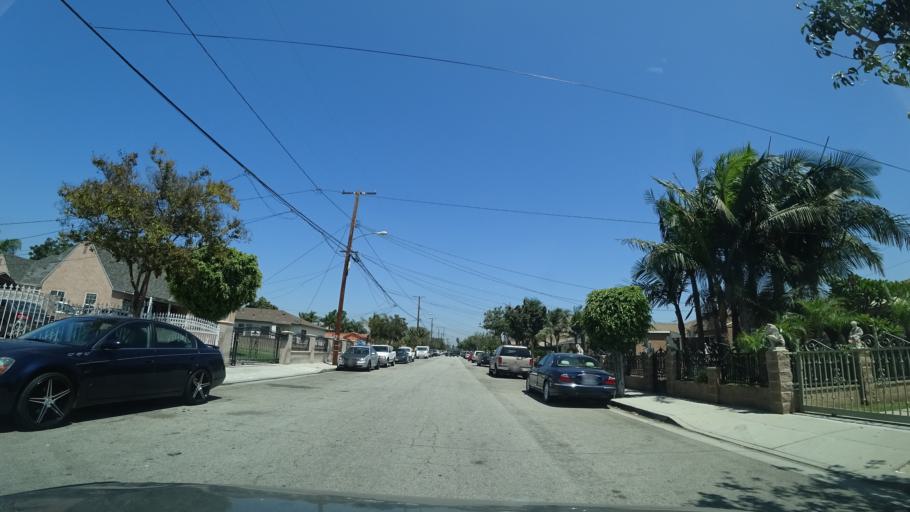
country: US
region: California
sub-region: Los Angeles County
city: Lennox
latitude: 33.9389
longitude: -118.3602
